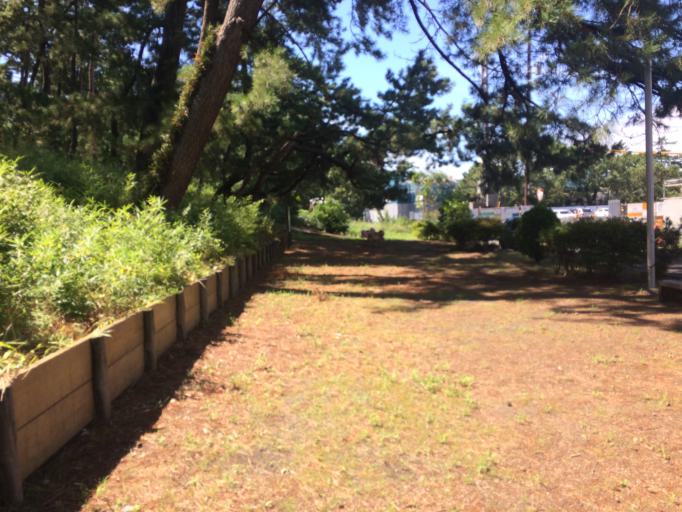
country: JP
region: Shizuoka
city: Shizuoka-shi
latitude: 34.9962
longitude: 138.5238
